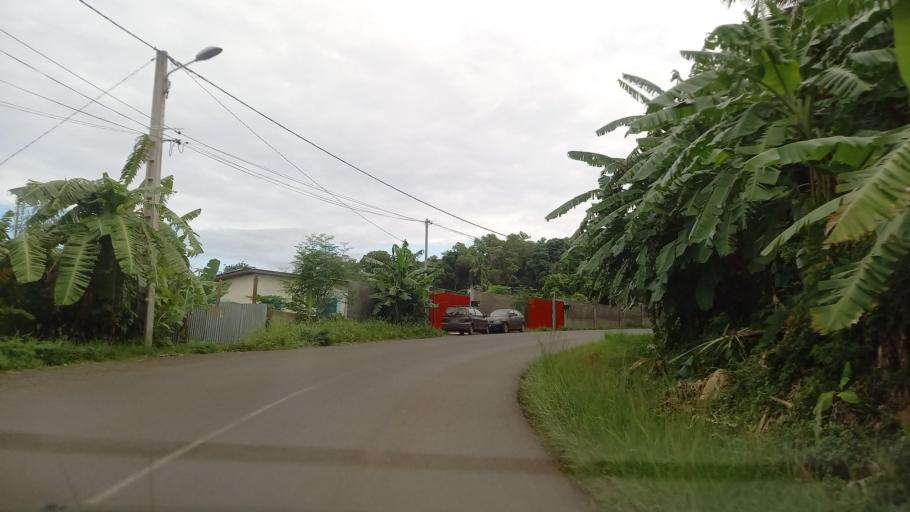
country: YT
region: Sada
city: Sada
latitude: -12.8545
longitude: 45.1035
